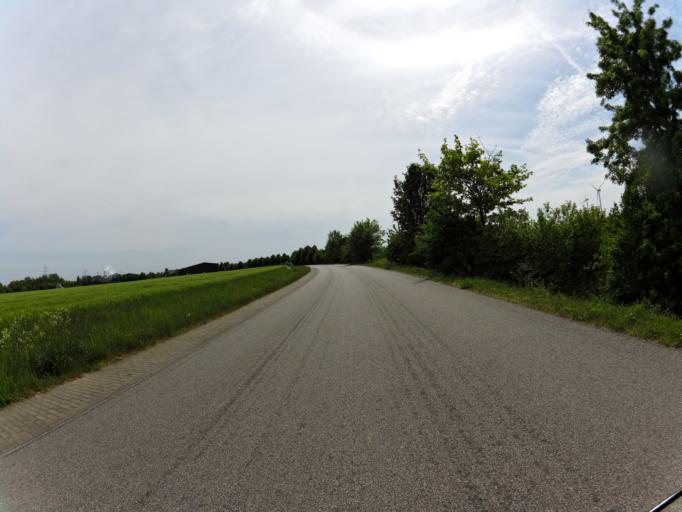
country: DE
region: North Rhine-Westphalia
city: Niedermerz
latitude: 50.8749
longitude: 6.2667
